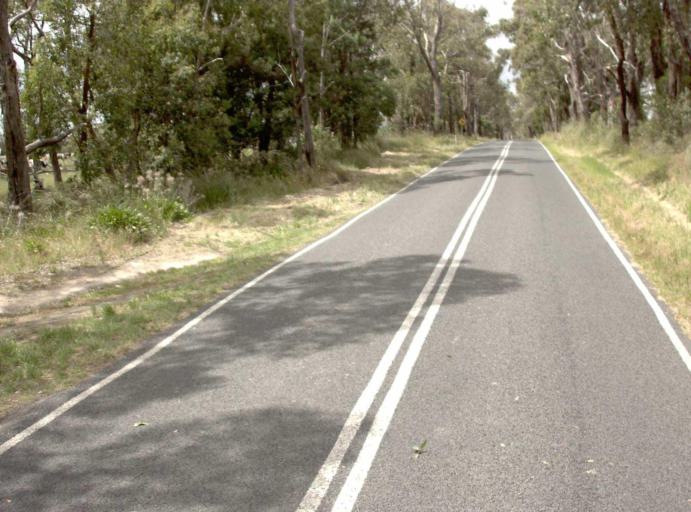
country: AU
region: Victoria
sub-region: Latrobe
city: Moe
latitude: -38.1243
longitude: 146.1481
